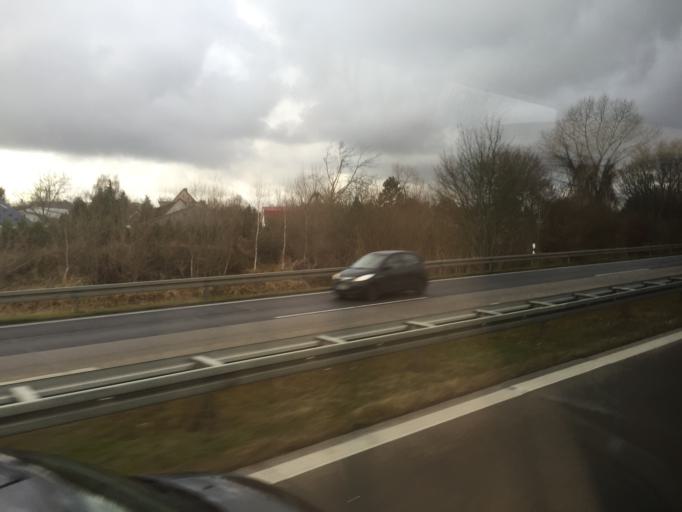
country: DE
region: Berlin
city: Buchholz
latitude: 52.6173
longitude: 13.4408
